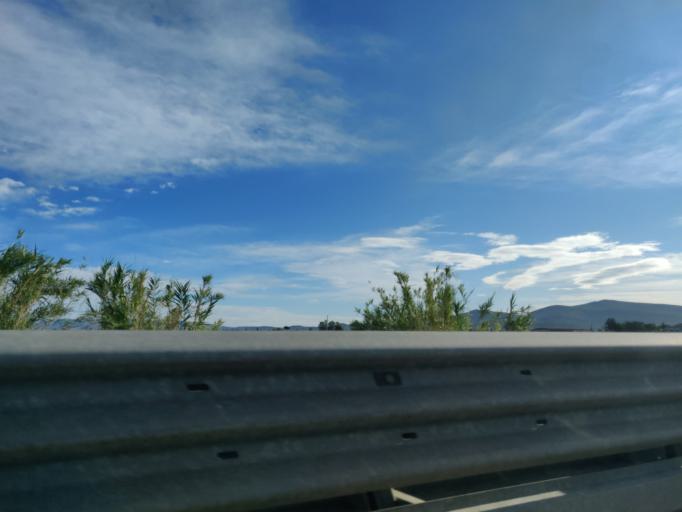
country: IT
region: Tuscany
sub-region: Provincia di Grosseto
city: Braccagni
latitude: 42.8951
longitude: 11.0577
